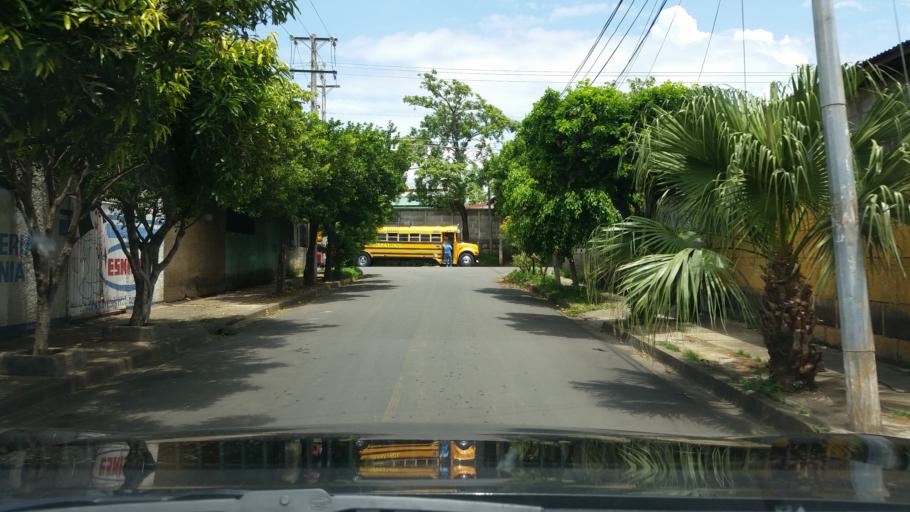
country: NI
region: Managua
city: Managua
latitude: 12.1241
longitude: -86.2481
